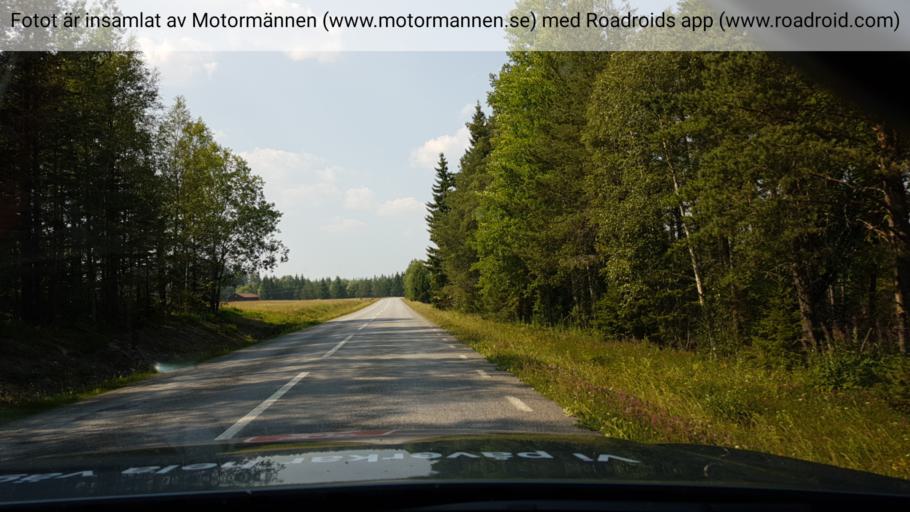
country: SE
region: Jaemtland
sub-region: Krokoms Kommun
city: Krokom
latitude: 63.1290
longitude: 14.2169
